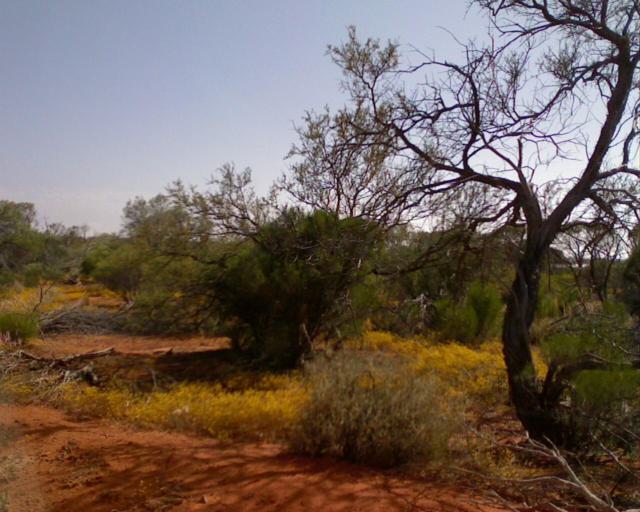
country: AU
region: Western Australia
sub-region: Merredin
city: Merredin
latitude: -30.9569
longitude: 118.8832
